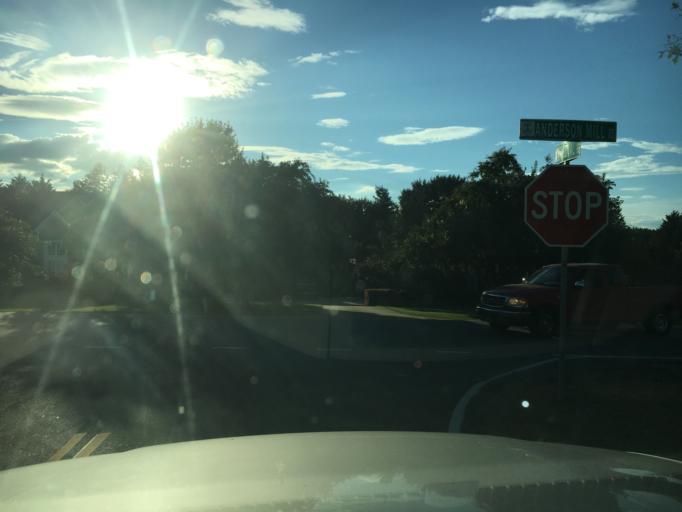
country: US
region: South Carolina
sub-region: Spartanburg County
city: Roebuck
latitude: 34.9022
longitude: -82.0064
